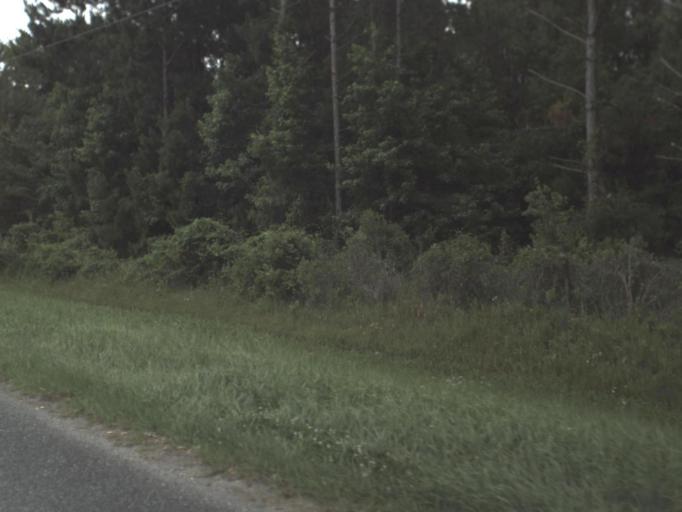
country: US
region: Florida
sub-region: Union County
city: Lake Butler
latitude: 29.9925
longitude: -82.2641
